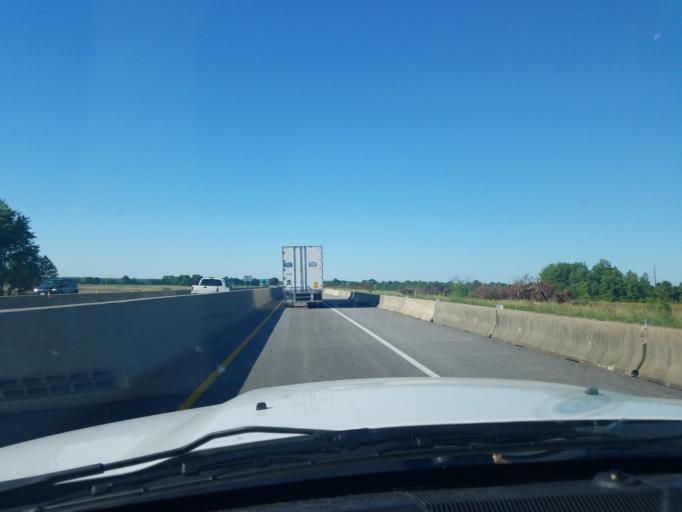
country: US
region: Kentucky
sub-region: Hardin County
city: Elizabethtown
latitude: 37.5876
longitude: -85.8706
